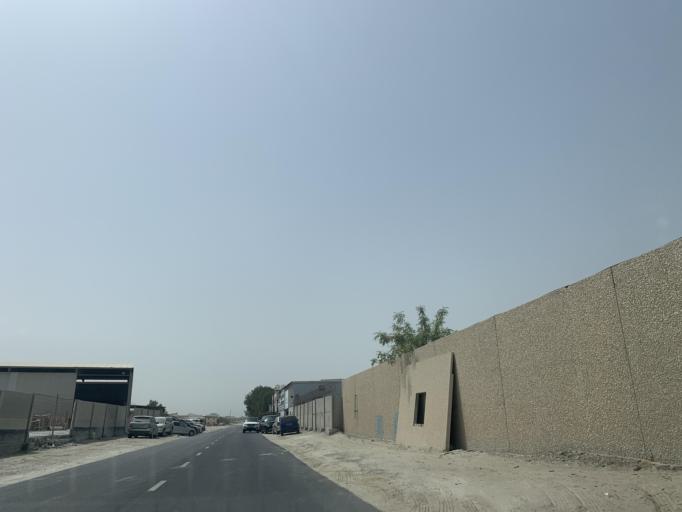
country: BH
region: Northern
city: Madinat `Isa
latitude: 26.1921
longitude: 50.5310
